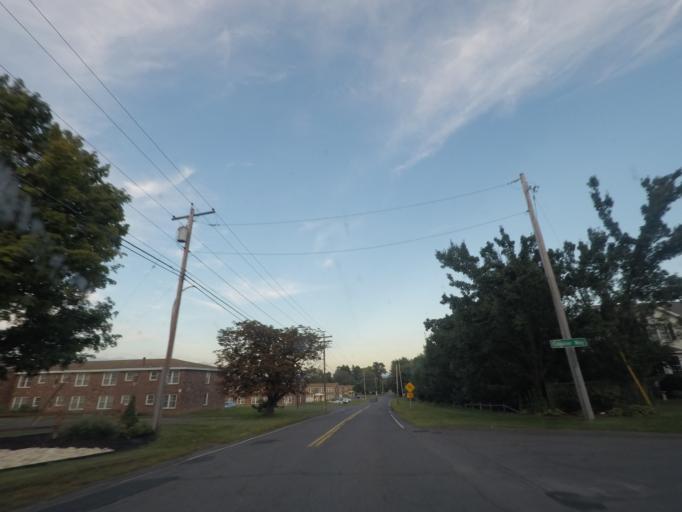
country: US
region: New York
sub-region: Schenectady County
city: Niskayuna
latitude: 42.7662
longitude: -73.7751
